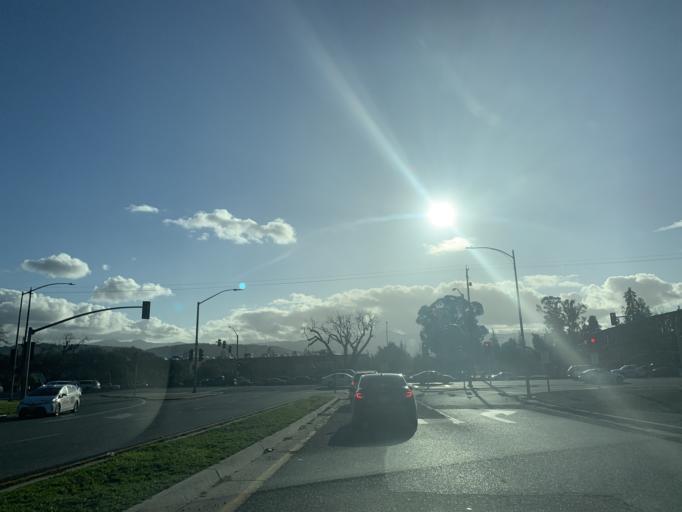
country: US
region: California
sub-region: Santa Clara County
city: Seven Trees
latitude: 37.2556
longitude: -121.8009
